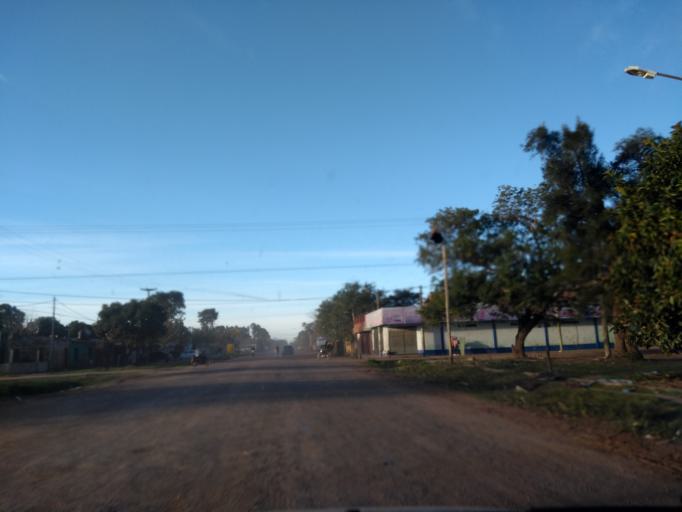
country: AR
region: Chaco
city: Resistencia
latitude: -27.4948
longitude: -58.9779
